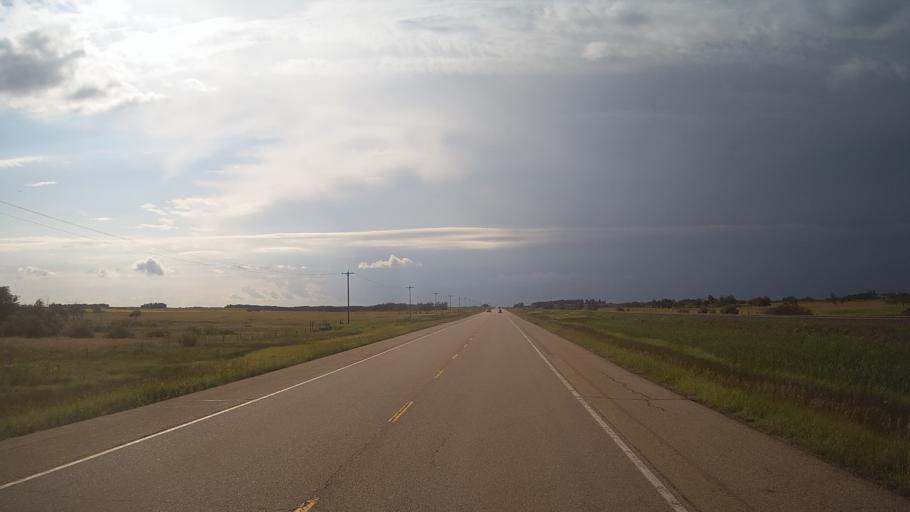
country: CA
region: Alberta
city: Viking
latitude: 53.1535
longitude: -111.9803
